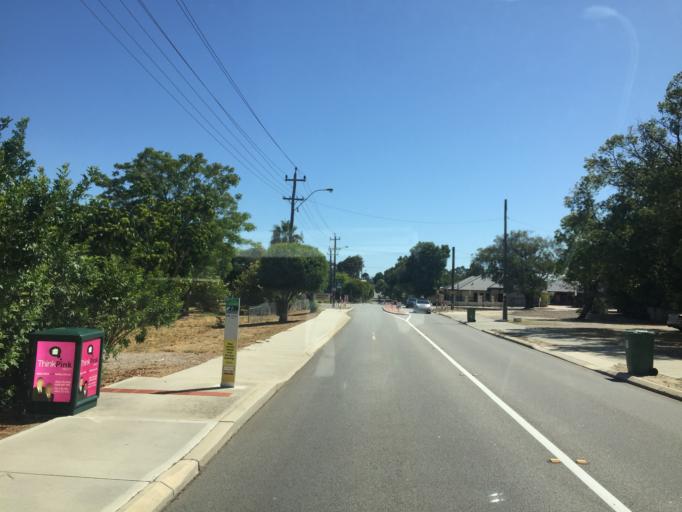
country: AU
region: Western Australia
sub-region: Belmont
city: Redcliffe
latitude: -31.9377
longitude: 115.9443
